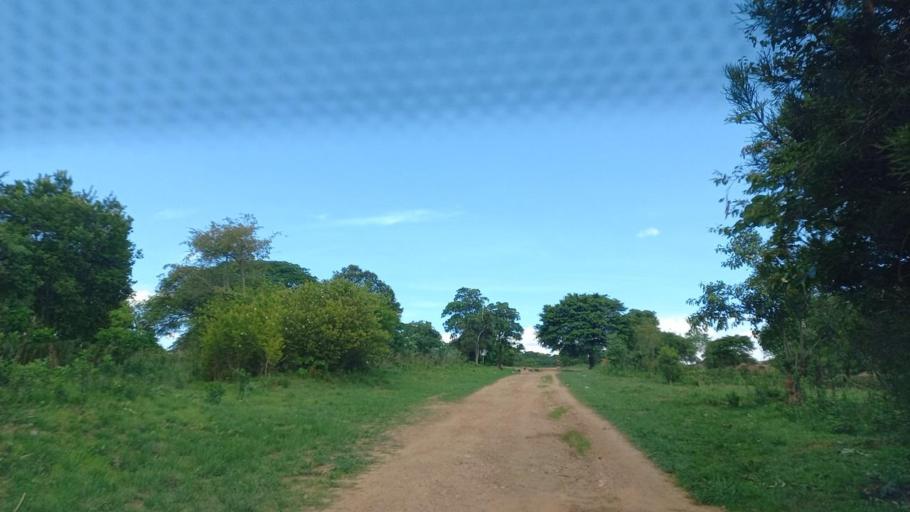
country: ZM
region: North-Western
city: Mwinilunga
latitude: -12.3584
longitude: 24.2334
